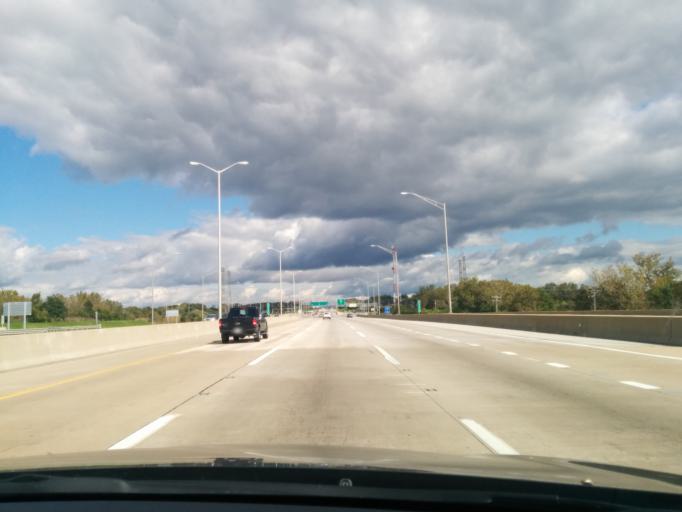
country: US
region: Illinois
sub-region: Kane County
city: North Aurora
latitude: 41.7963
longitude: -88.3169
